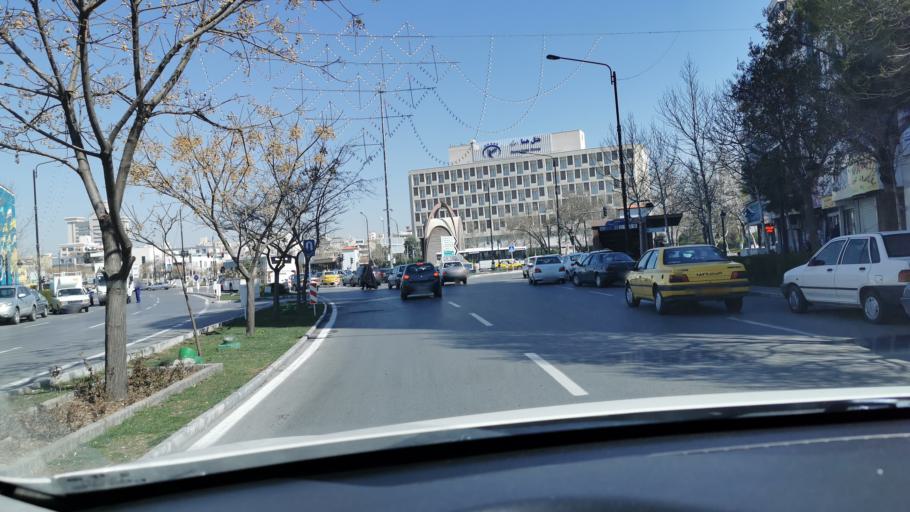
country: IR
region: Razavi Khorasan
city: Mashhad
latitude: 36.2960
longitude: 59.5731
